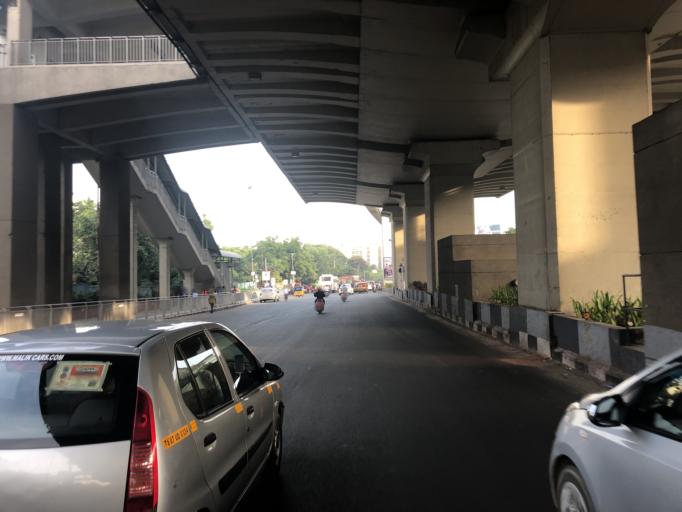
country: IN
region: Telangana
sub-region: Rangareddi
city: Kukatpalli
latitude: 17.4416
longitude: 78.4417
